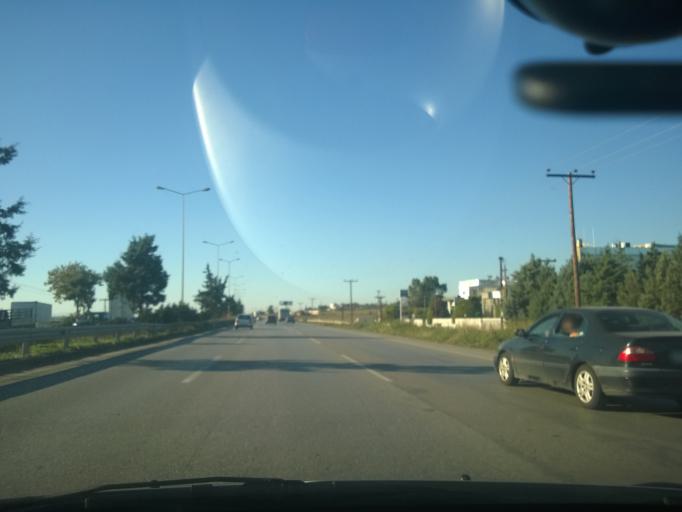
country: GR
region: Central Macedonia
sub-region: Nomos Thessalonikis
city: Thermi
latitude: 40.5494
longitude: 23.0022
